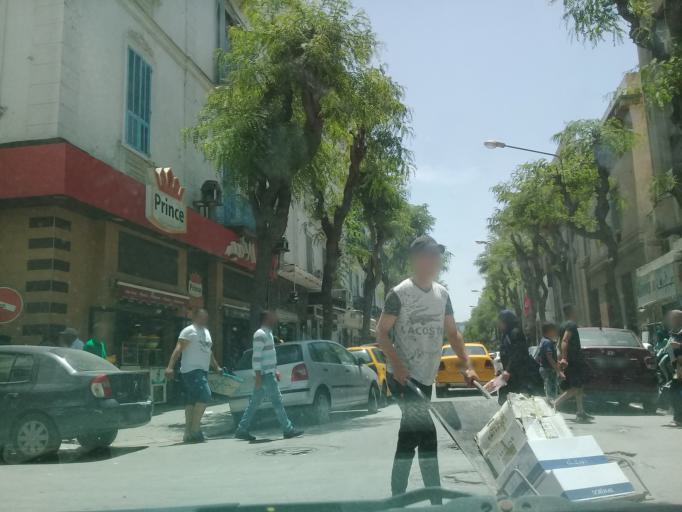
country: TN
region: Tunis
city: Tunis
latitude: 36.7972
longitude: 10.1789
